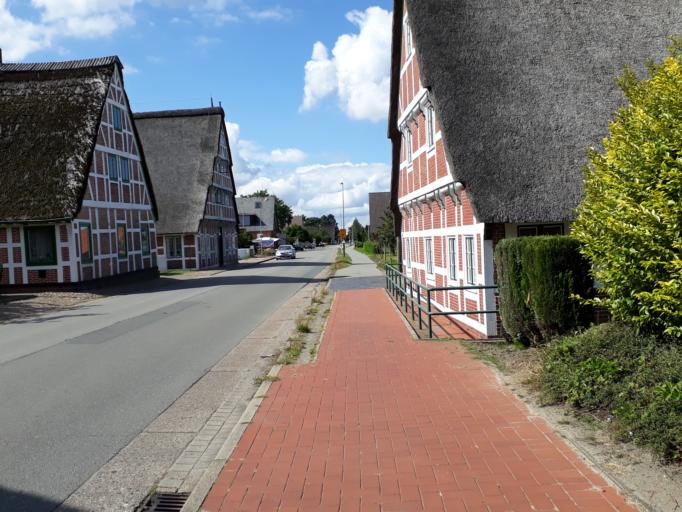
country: DE
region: Lower Saxony
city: Jork
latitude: 53.5345
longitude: 9.6733
